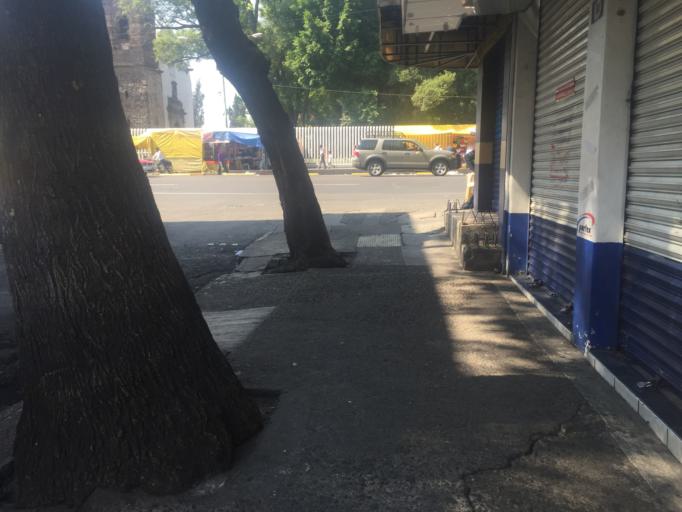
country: MX
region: Mexico City
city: Mexico City
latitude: 19.4265
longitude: -99.1298
